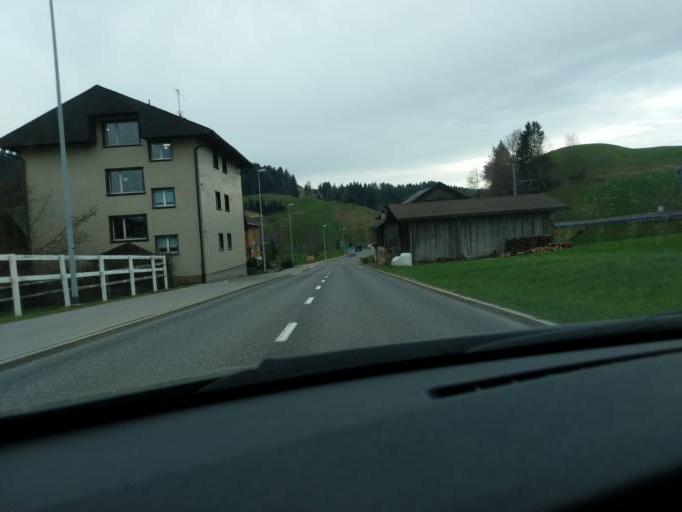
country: CH
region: Lucerne
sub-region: Entlebuch District
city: Escholzmatt
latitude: 46.9060
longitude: 7.9302
